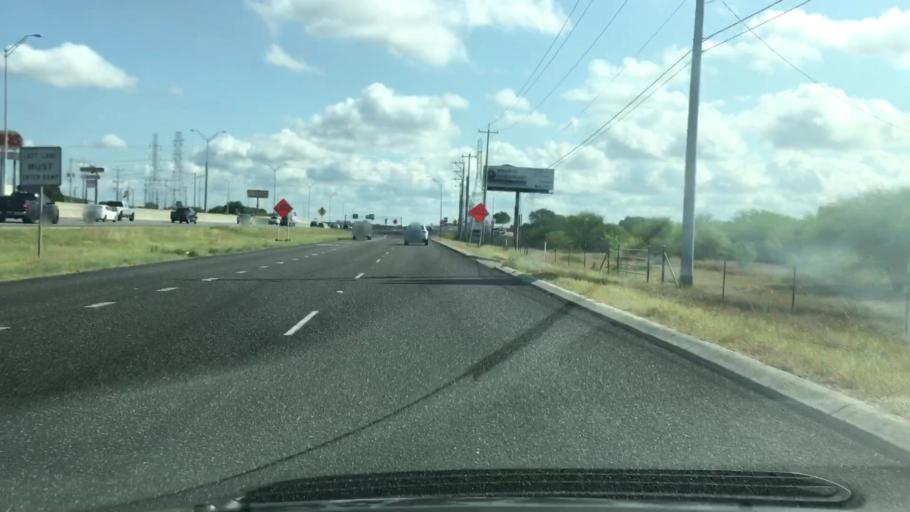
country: US
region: Texas
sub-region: Bexar County
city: Selma
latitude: 29.6046
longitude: -98.2712
